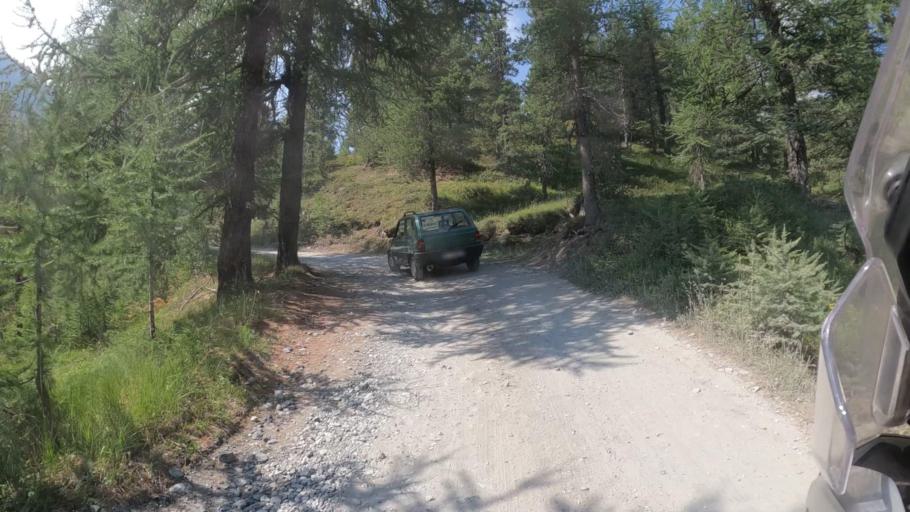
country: IT
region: Piedmont
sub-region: Provincia di Torino
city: Cesana Torinese
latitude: 44.9148
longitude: 6.8013
